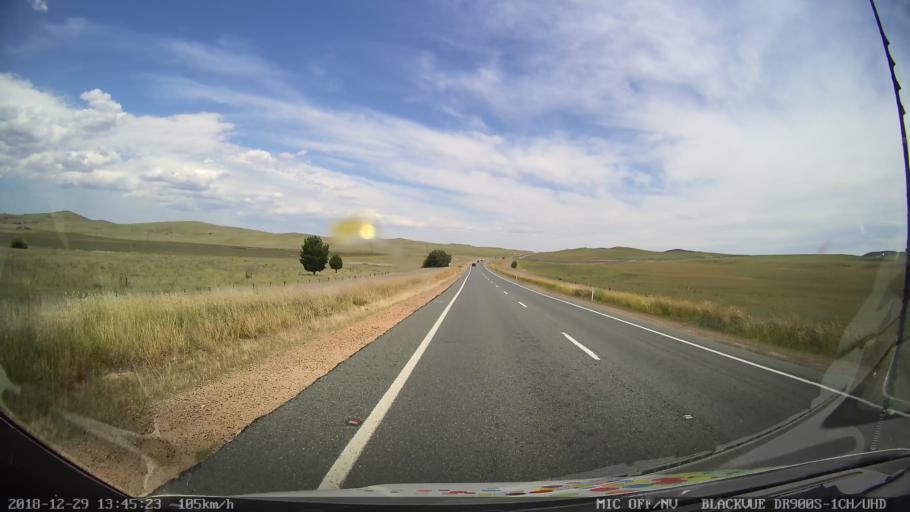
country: AU
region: New South Wales
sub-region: Cooma-Monaro
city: Cooma
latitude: -36.0956
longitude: 149.1452
